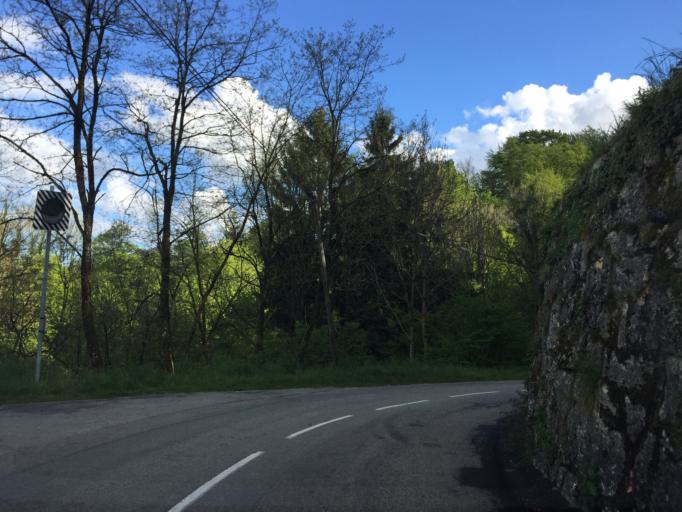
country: FR
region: Rhone-Alpes
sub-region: Departement de la Savoie
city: Vimines
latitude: 45.5644
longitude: 5.8456
